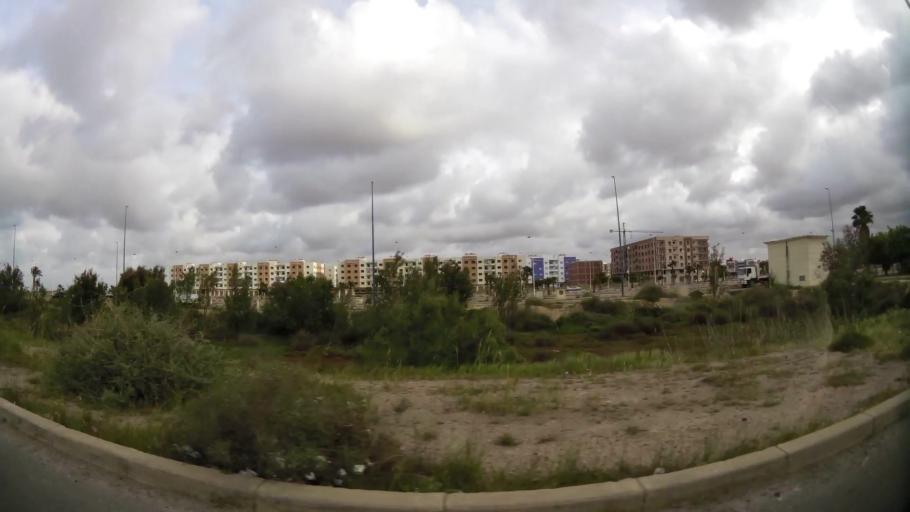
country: MA
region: Oriental
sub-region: Nador
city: Nador
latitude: 35.1548
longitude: -2.9101
